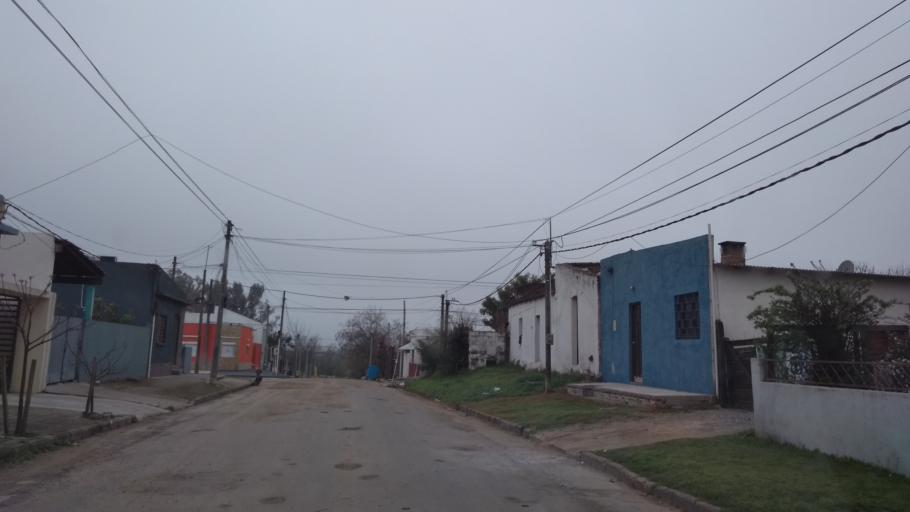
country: UY
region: Florida
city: Florida
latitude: -34.0947
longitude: -56.2084
